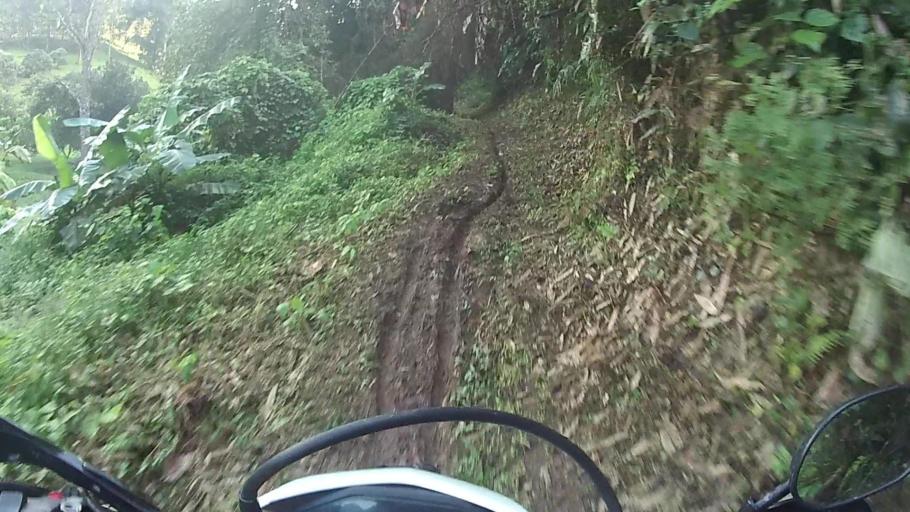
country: TH
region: Chiang Mai
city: Mae On
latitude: 18.9280
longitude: 99.2938
